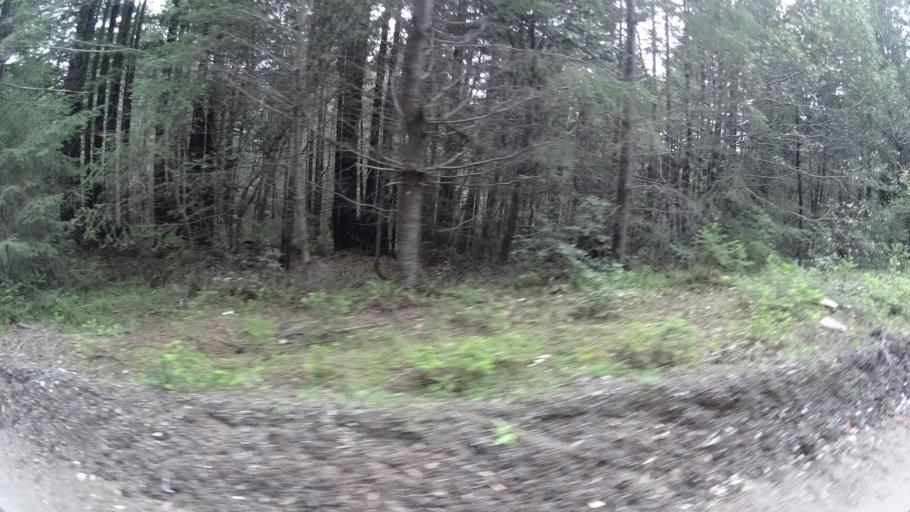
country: US
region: California
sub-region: Humboldt County
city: Redway
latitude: 40.3152
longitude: -123.8315
